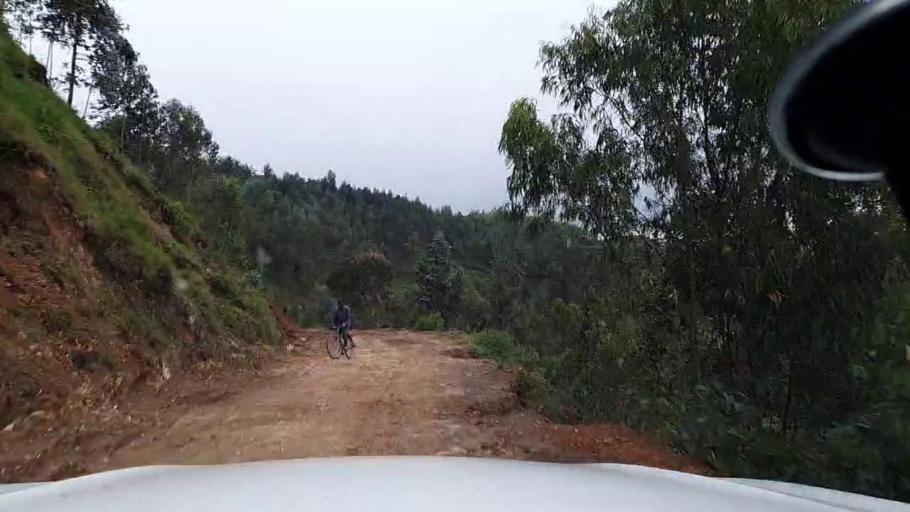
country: RW
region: Western Province
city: Kibuye
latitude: -2.0851
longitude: 29.5042
